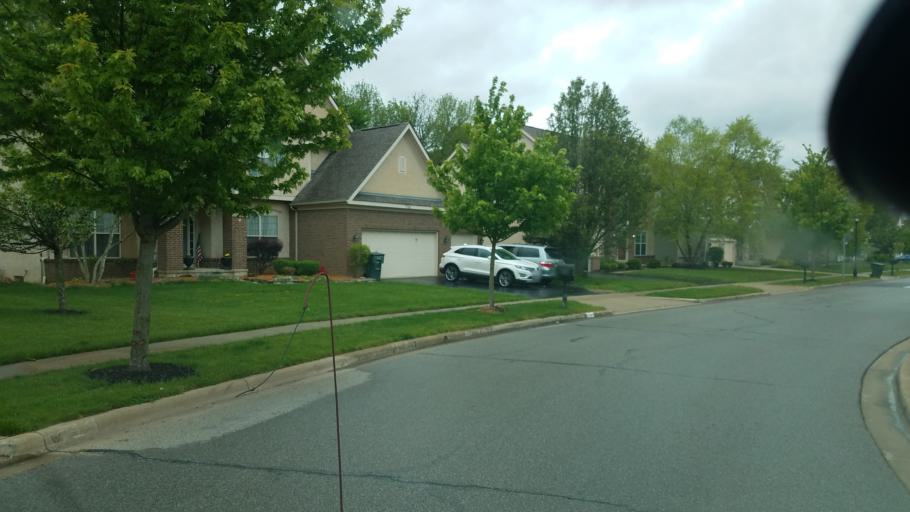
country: US
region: Ohio
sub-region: Franklin County
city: Worthington
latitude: 40.1195
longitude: -83.0428
